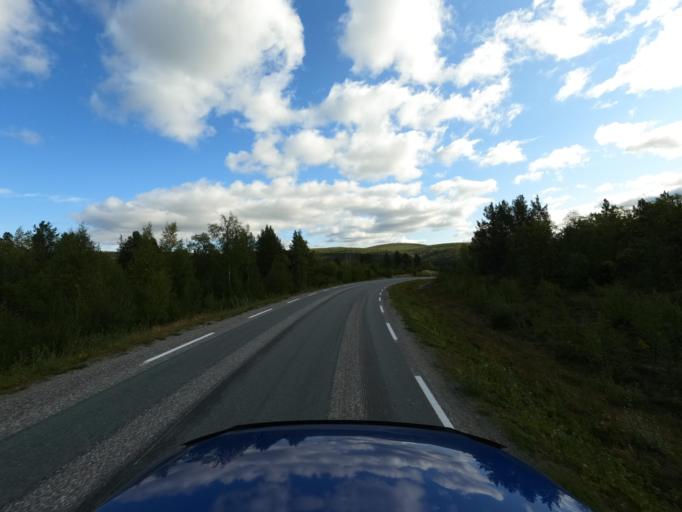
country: NO
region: Finnmark Fylke
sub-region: Karasjok
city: Karasjohka
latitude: 69.4298
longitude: 25.7906
